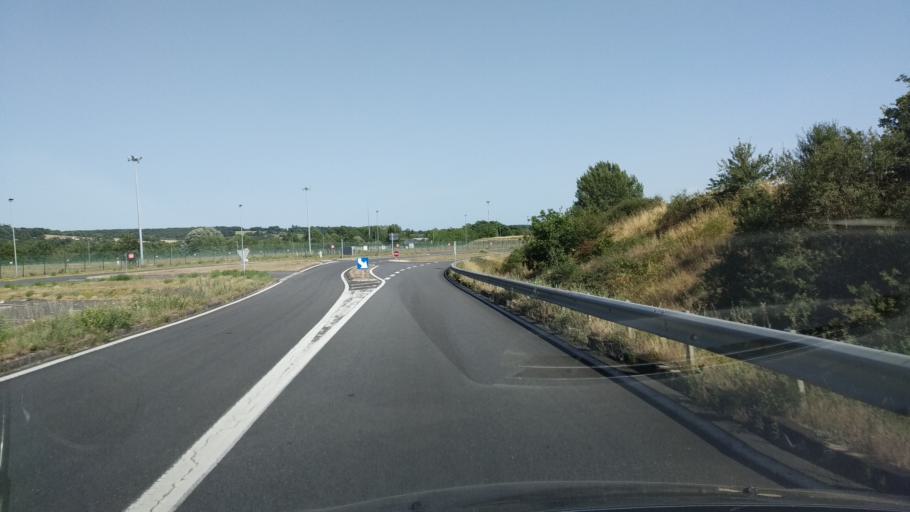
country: FR
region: Poitou-Charentes
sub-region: Departement de la Vienne
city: Lussac-les-Chateaux
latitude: 46.4479
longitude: 0.6526
